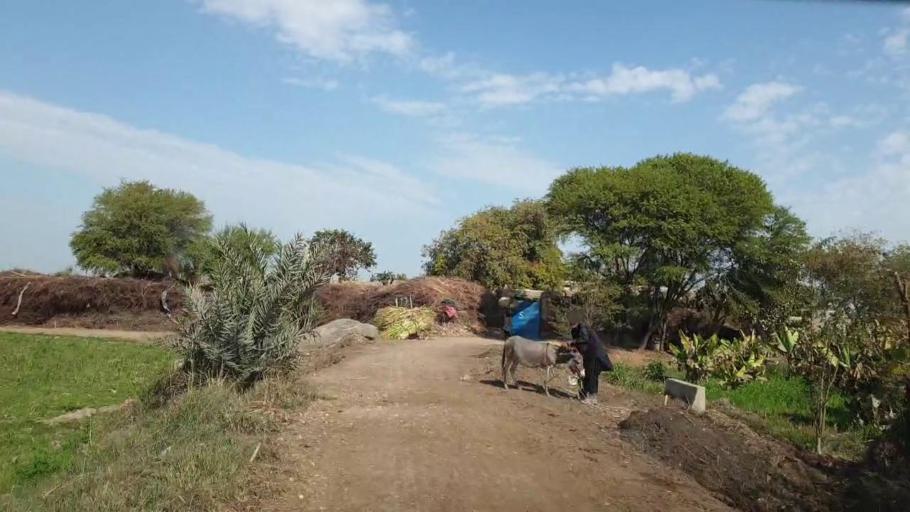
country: PK
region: Sindh
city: Matiari
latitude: 25.5606
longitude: 68.4581
